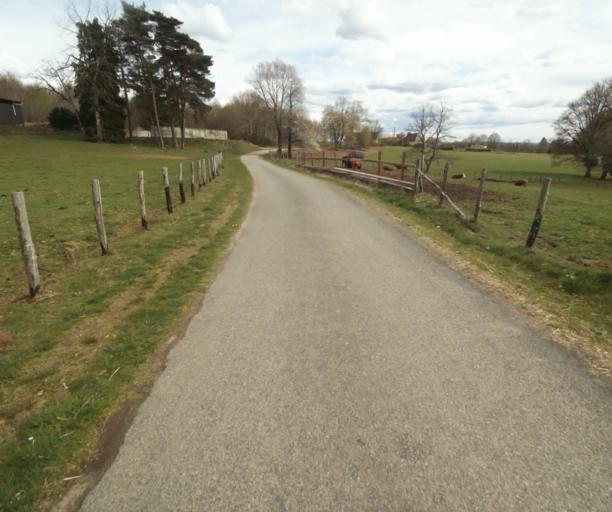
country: FR
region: Limousin
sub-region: Departement de la Correze
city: Argentat
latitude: 45.1853
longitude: 1.9193
